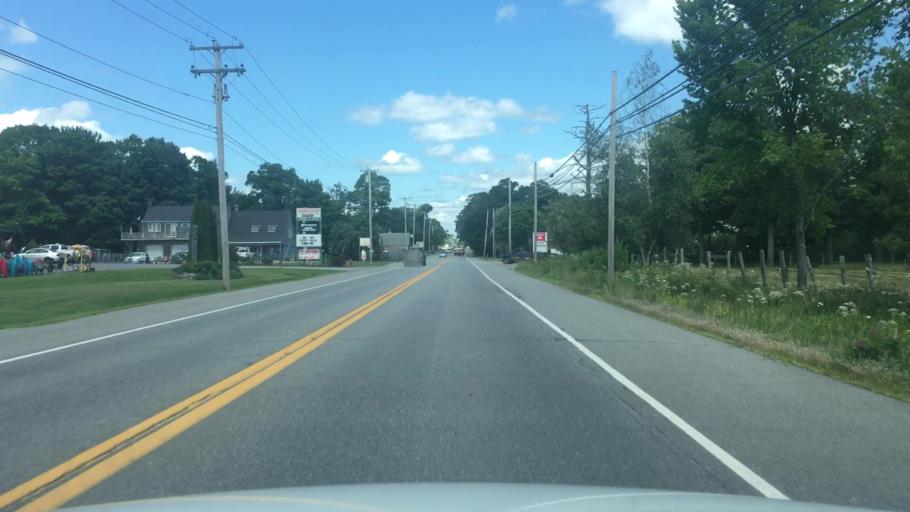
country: US
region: Maine
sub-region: Waldo County
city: Belfast
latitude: 44.4018
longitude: -68.9887
